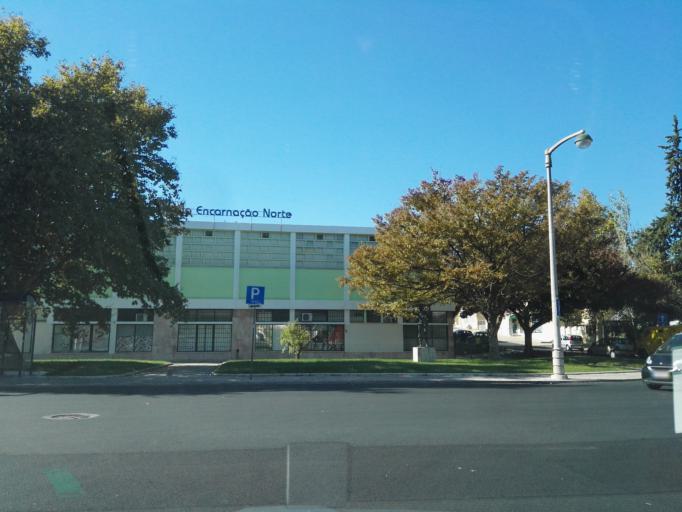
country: PT
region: Lisbon
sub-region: Loures
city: Moscavide
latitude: 38.7771
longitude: -9.1178
